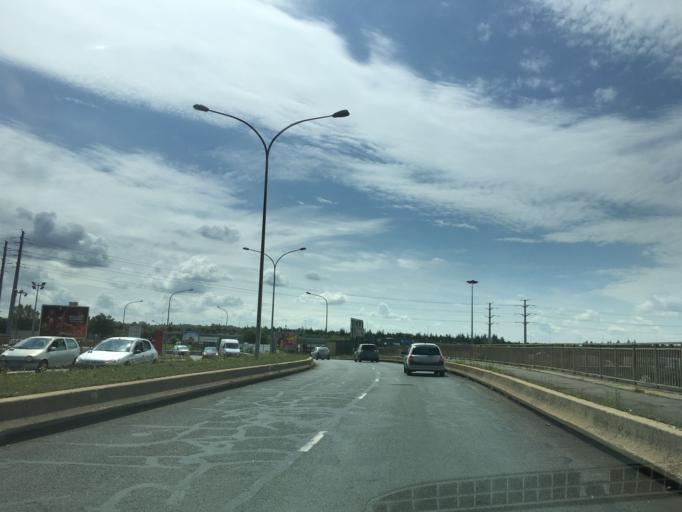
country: FR
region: Ile-de-France
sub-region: Departement du Val-de-Marne
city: Bonneuil-sur-Marne
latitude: 48.7619
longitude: 2.4791
